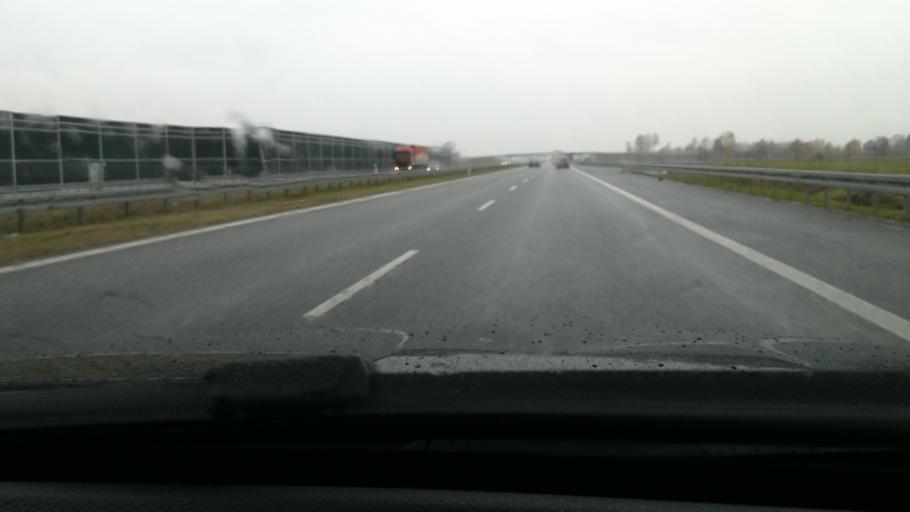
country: PL
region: Masovian Voivodeship
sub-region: Powiat zyrardowski
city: Guzow
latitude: 52.0740
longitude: 20.2691
